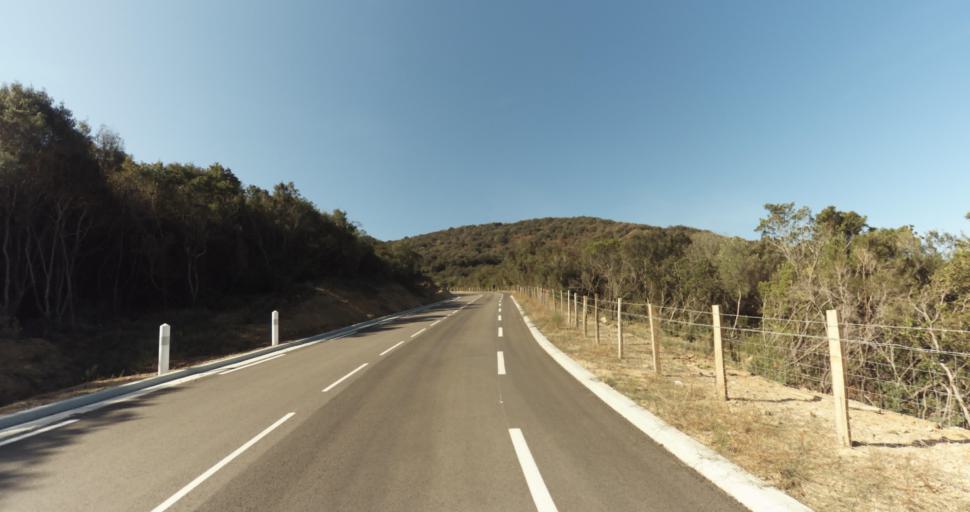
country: FR
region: Corsica
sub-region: Departement de la Corse-du-Sud
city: Ajaccio
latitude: 41.9261
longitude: 8.6488
